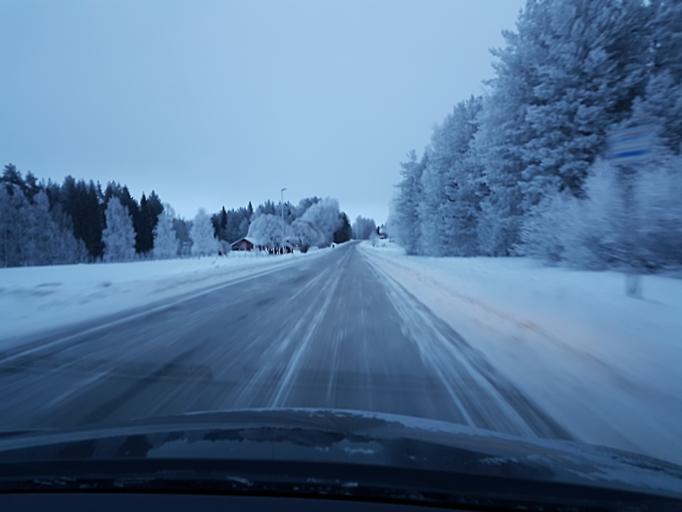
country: SE
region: Norrbotten
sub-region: Pitea Kommun
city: Roknas
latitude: 65.3479
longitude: 21.1120
